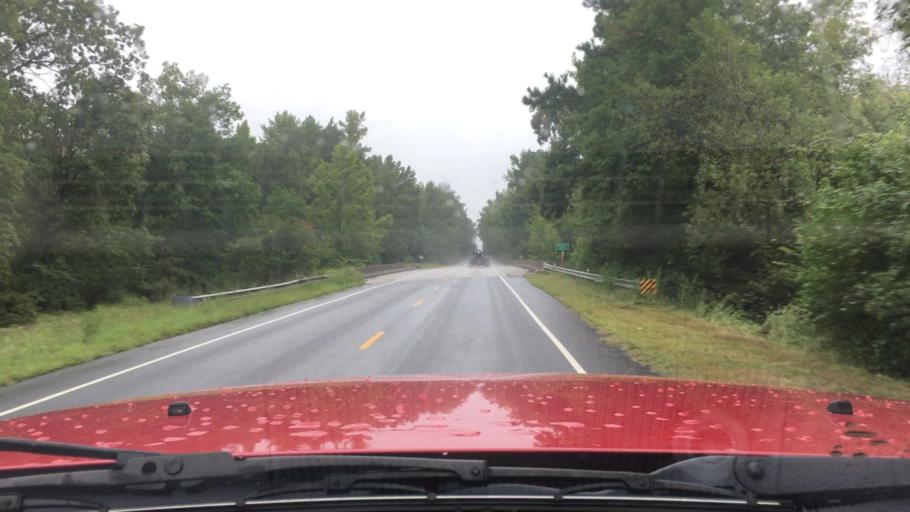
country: US
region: Virginia
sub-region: Caroline County
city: Bowling Green
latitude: 37.9648
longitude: -77.3426
